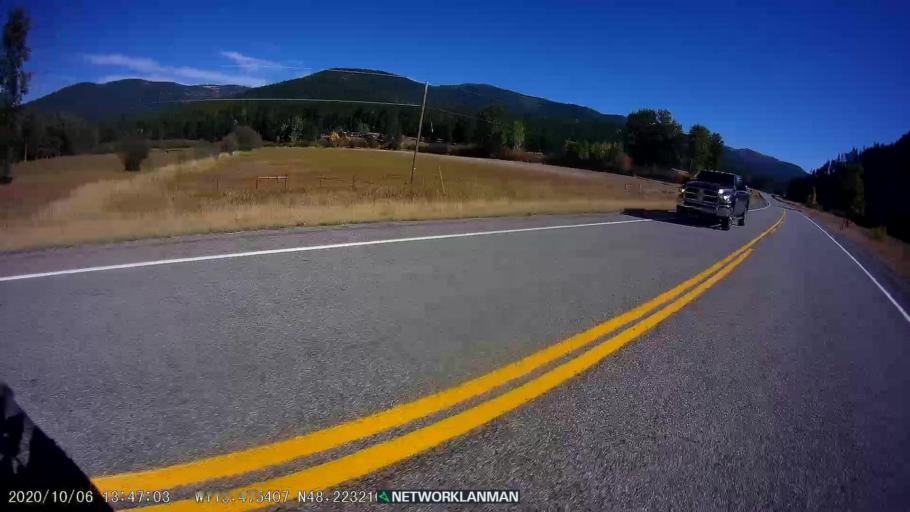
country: US
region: Montana
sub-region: Lincoln County
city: Libby
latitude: 48.2230
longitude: -115.4750
